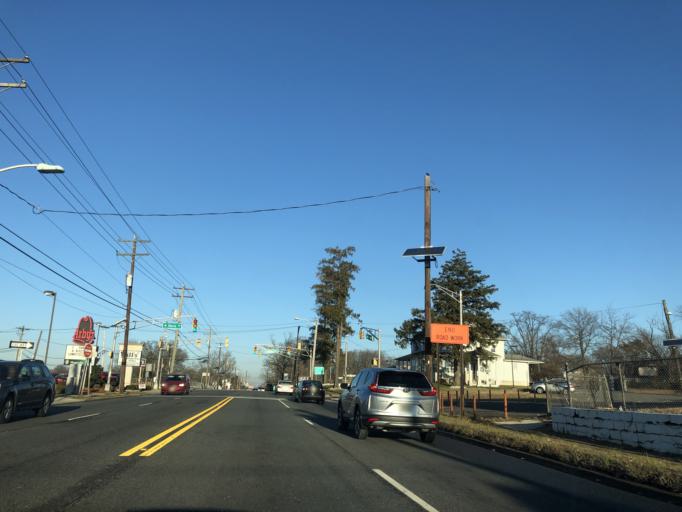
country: US
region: New Jersey
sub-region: Camden County
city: Lawnside
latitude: 39.8624
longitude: -75.0345
